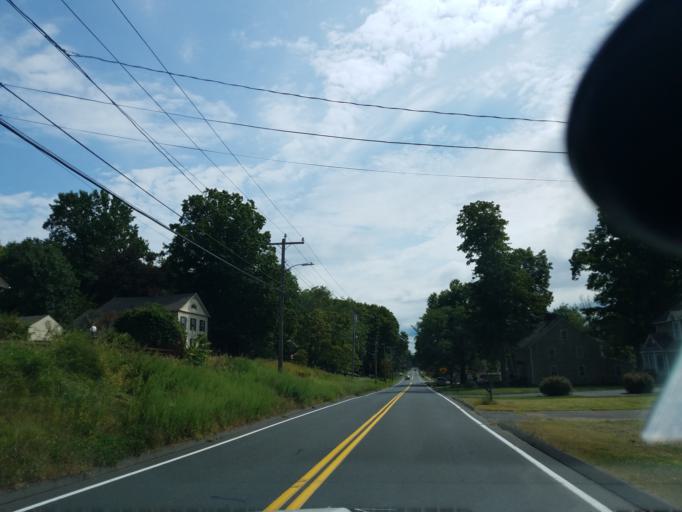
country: US
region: Connecticut
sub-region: Hartford County
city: Wethersfield
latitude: 41.6745
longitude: -72.6426
